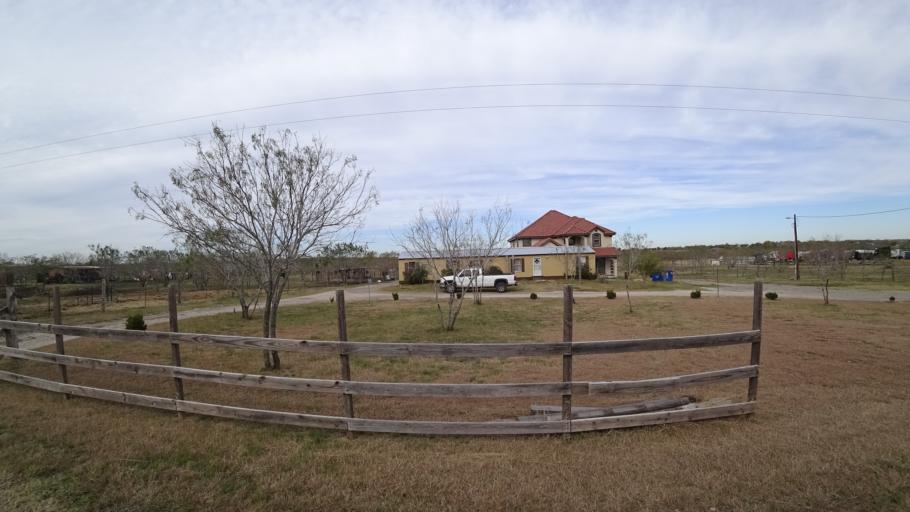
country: US
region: Texas
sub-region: Travis County
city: Garfield
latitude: 30.1131
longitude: -97.5935
